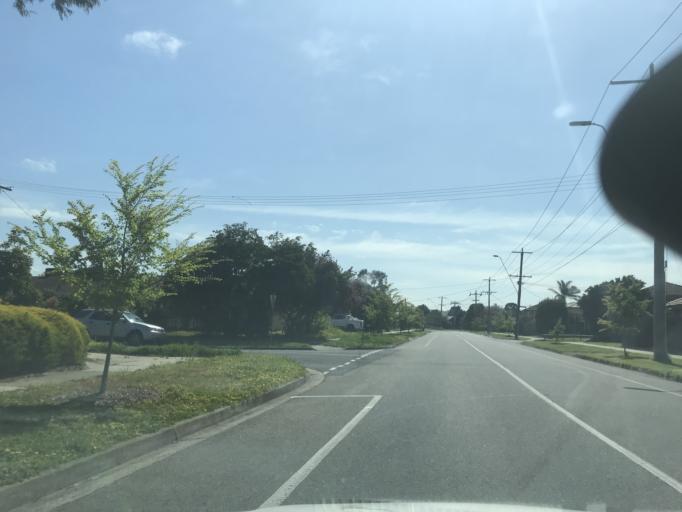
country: AU
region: Victoria
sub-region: Whittlesea
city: Epping
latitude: -37.6473
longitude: 145.0358
